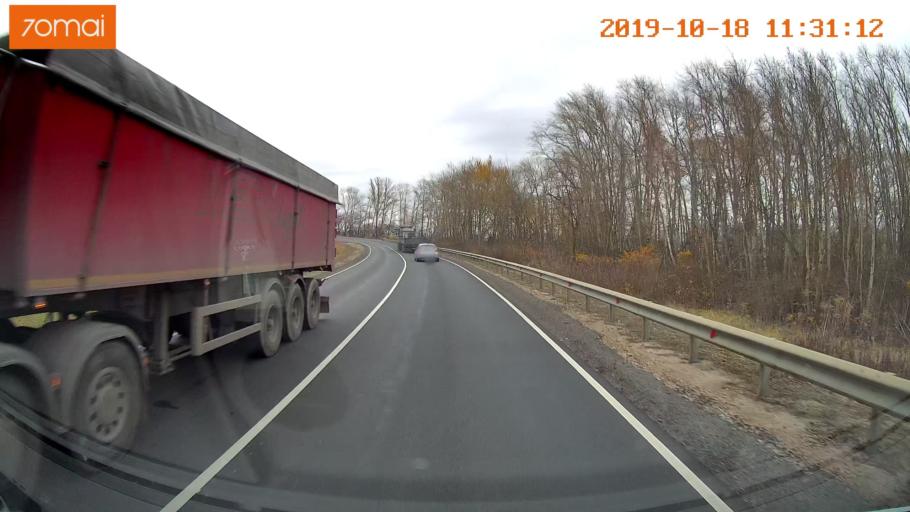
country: RU
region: Rjazan
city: Oktyabr'skiy
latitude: 54.1418
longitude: 38.6918
